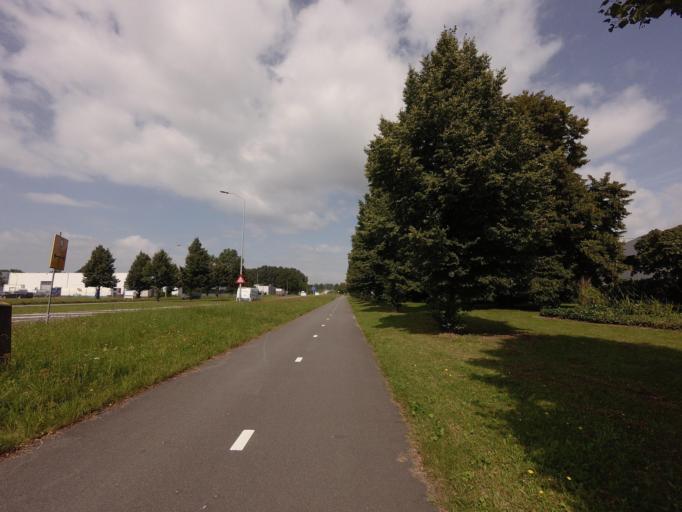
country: NL
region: Flevoland
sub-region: Gemeente Lelystad
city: Lelystad
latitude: 52.5428
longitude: 5.5219
